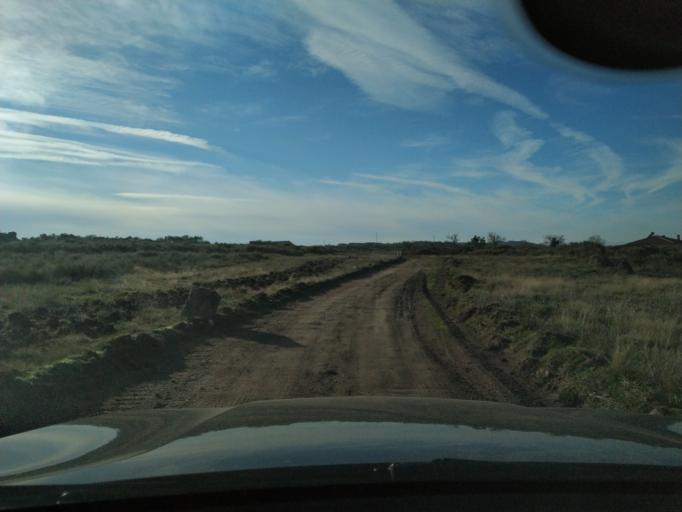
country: PT
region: Vila Real
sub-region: Sabrosa
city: Sabrosa
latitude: 41.3073
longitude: -7.6089
